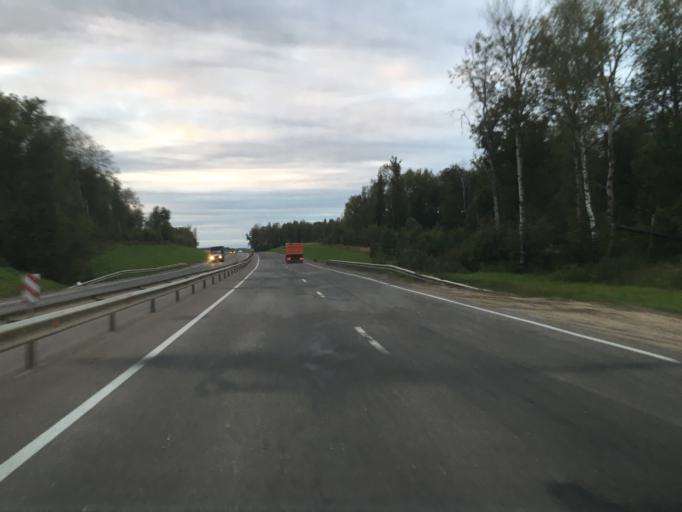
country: RU
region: Kaluga
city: Kaluga
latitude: 54.6083
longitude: 36.3114
